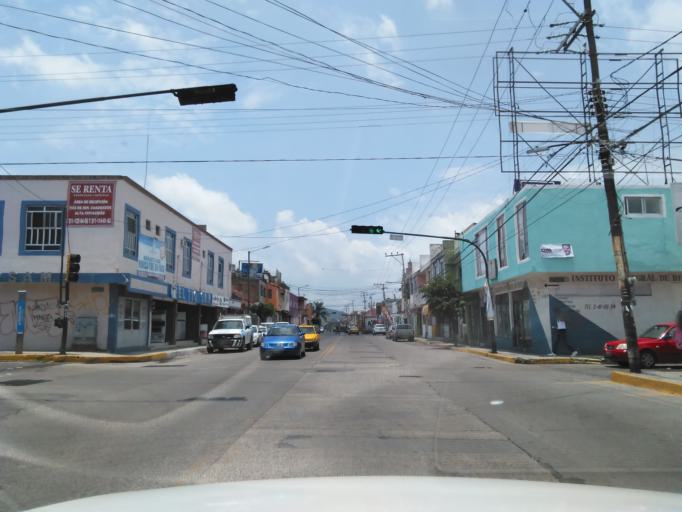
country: MX
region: Nayarit
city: Tepic
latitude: 21.5086
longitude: -104.8873
